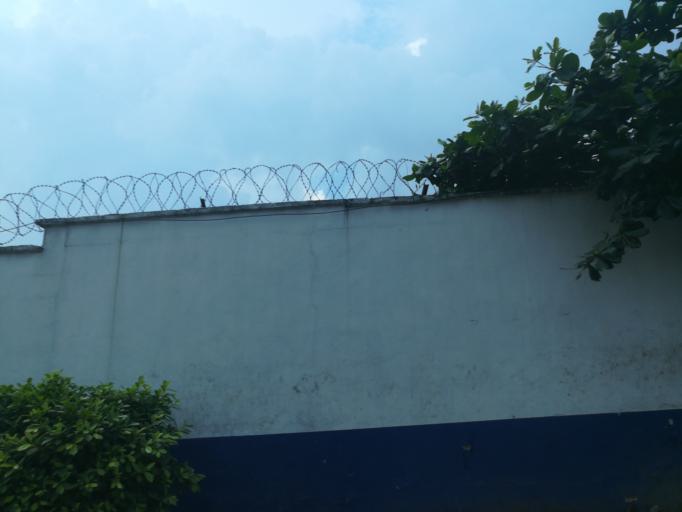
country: NG
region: Lagos
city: Ikeja
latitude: 6.6053
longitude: 3.3654
